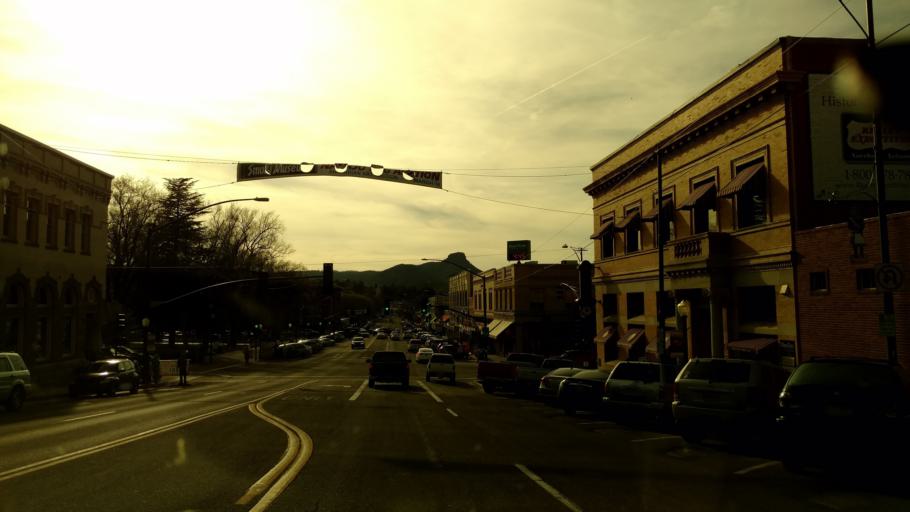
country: US
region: Arizona
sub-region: Yavapai County
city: Prescott
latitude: 34.5419
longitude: -112.4681
